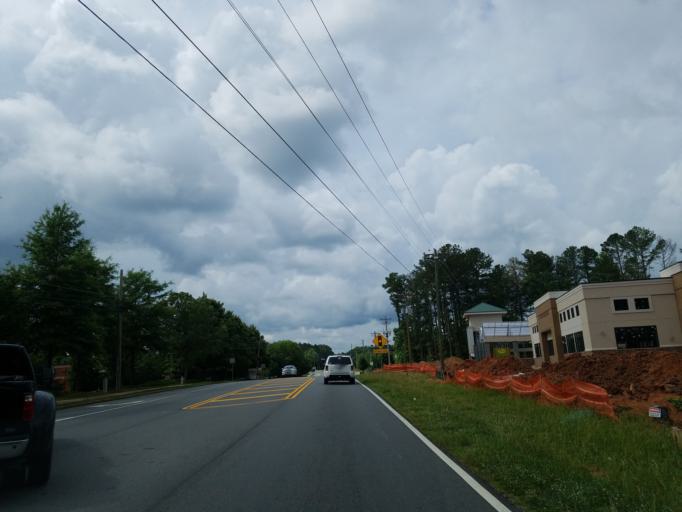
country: US
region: Georgia
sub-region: Fulton County
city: Milton
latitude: 34.1158
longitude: -84.2695
